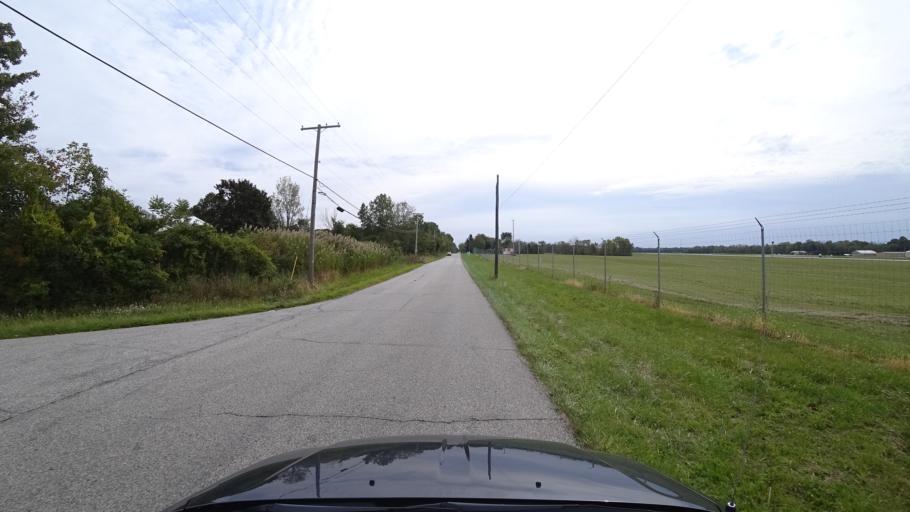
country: US
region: Indiana
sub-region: LaPorte County
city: Trail Creek
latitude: 41.7088
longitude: -86.8163
